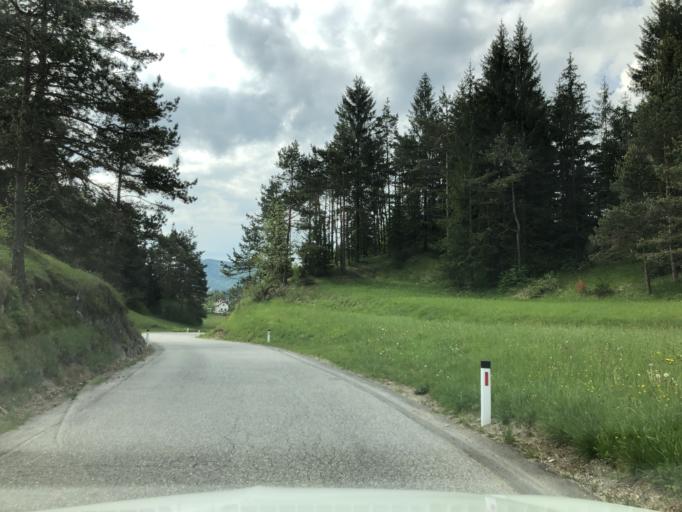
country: SI
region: Bloke
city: Nova Vas
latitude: 45.7814
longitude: 14.5016
